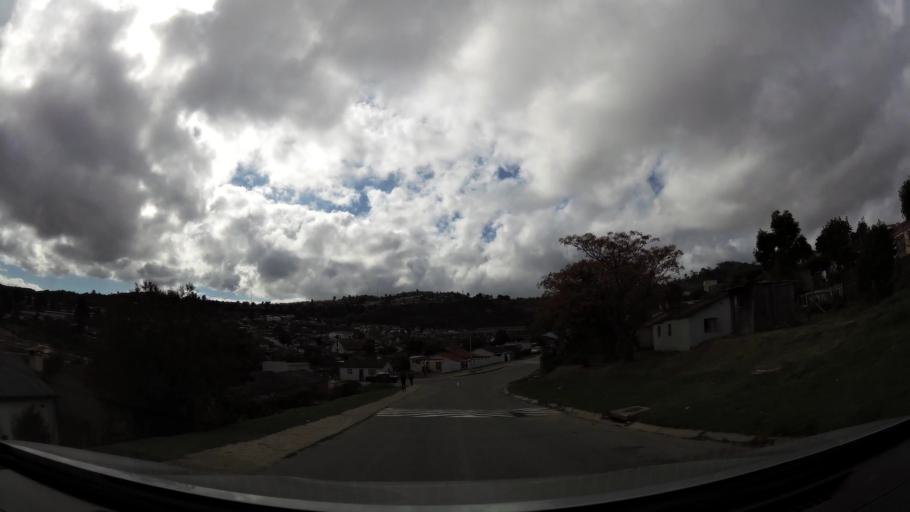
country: ZA
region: Western Cape
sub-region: Eden District Municipality
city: Knysna
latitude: -34.0512
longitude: 23.0963
